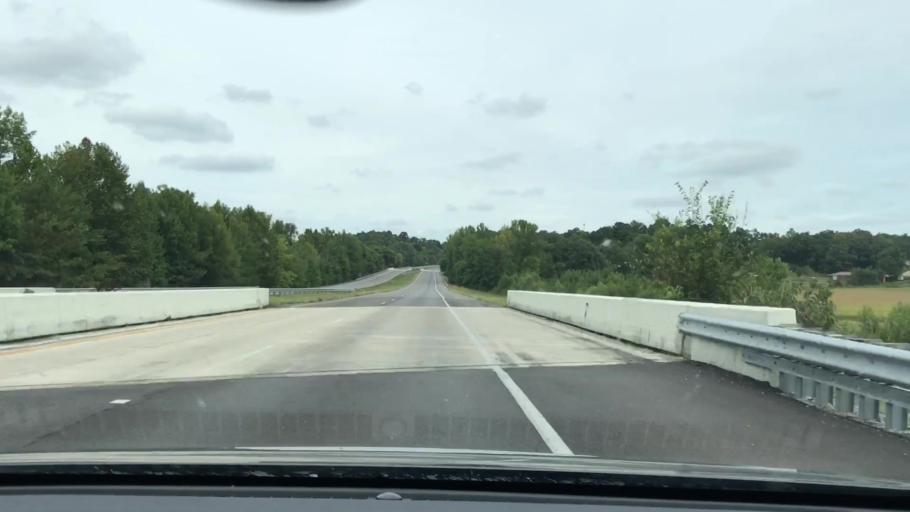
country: US
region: Kentucky
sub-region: Marshall County
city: Benton
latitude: 36.8111
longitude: -88.4898
